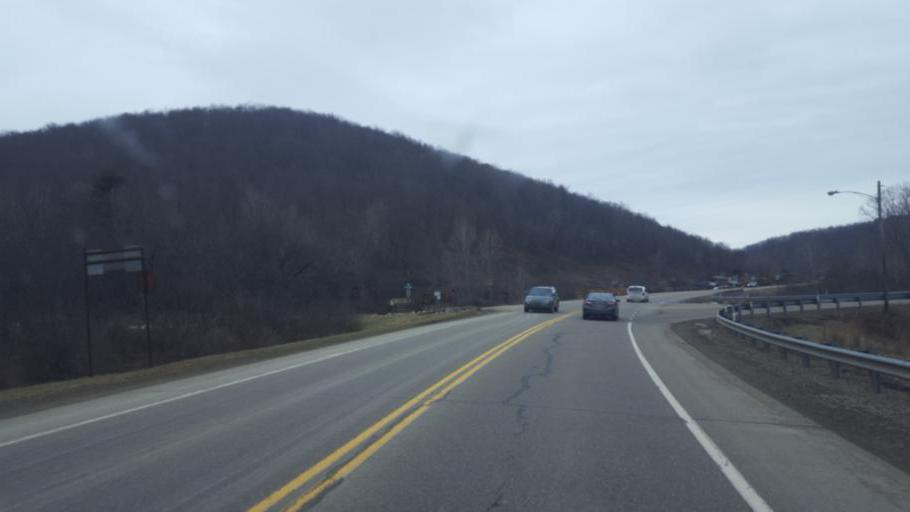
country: US
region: Pennsylvania
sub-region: Potter County
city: Coudersport
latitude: 41.7907
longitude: -78.0178
